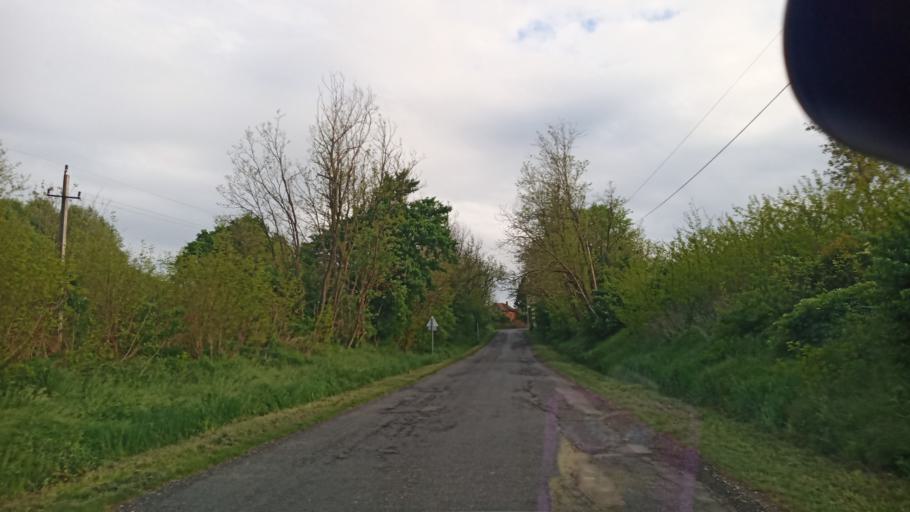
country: HU
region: Zala
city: Pacsa
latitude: 46.7305
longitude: 17.0037
